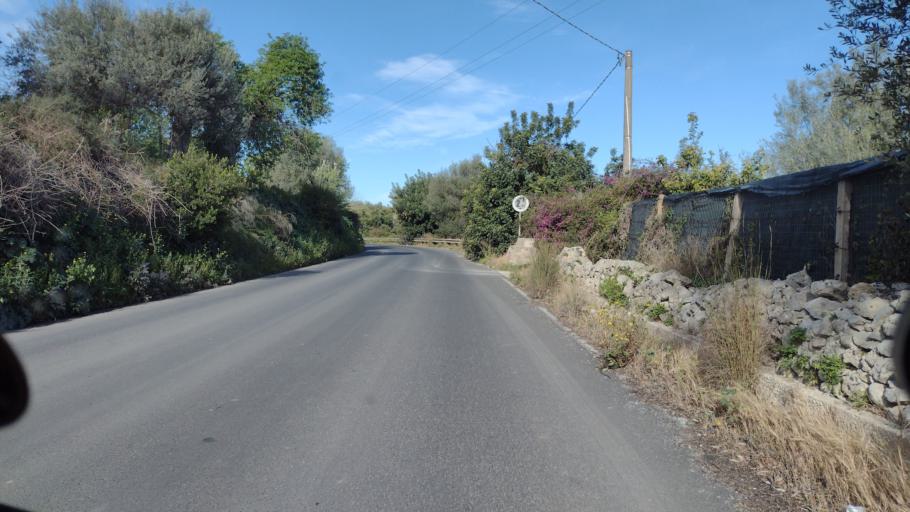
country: IT
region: Sicily
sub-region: Provincia di Siracusa
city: Noto
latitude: 36.8772
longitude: 15.0954
